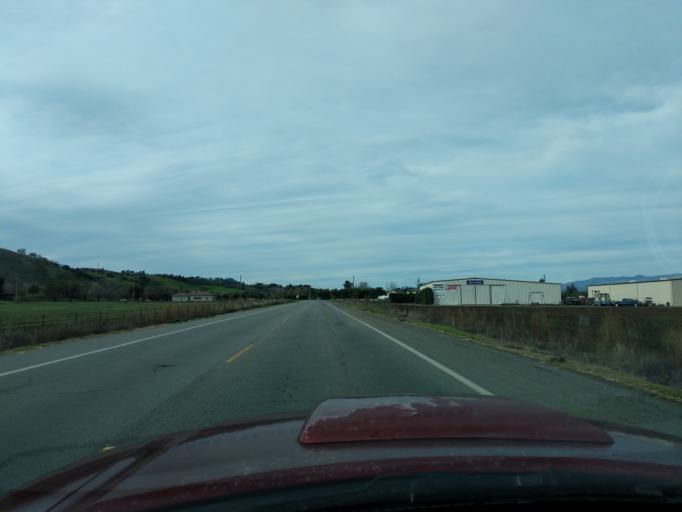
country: US
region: California
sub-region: Santa Clara County
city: San Martin
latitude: 37.0663
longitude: -121.6139
